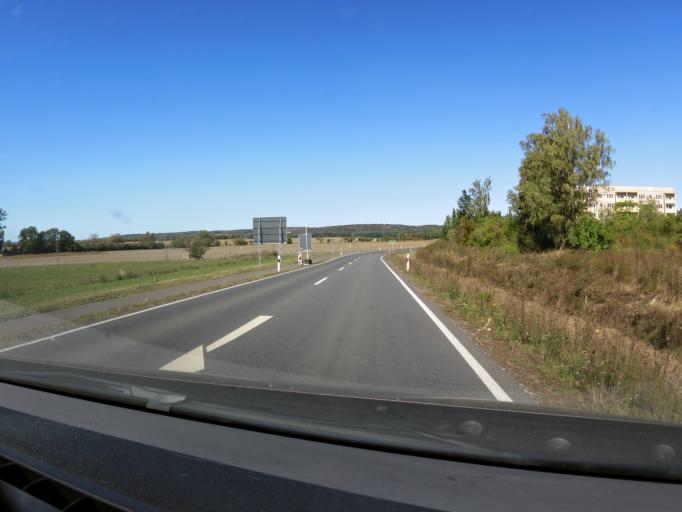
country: DE
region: Saxony-Anhalt
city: Bad Suderode
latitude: 51.7563
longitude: 11.1327
